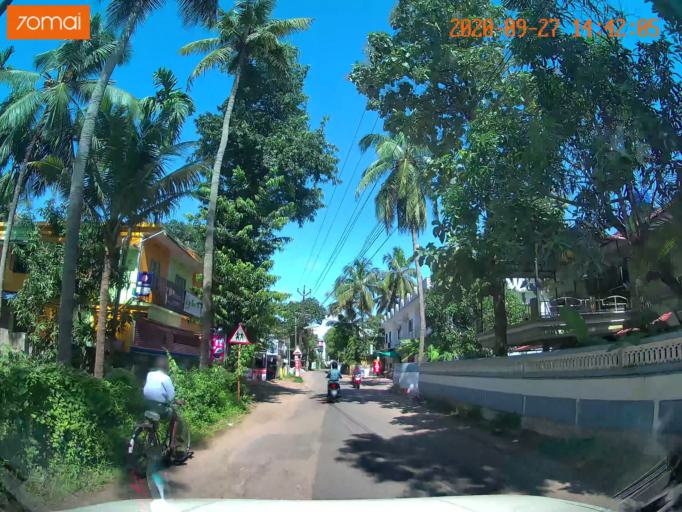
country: IN
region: Kerala
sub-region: Thrissur District
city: Thanniyam
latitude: 10.4400
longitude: 76.0919
